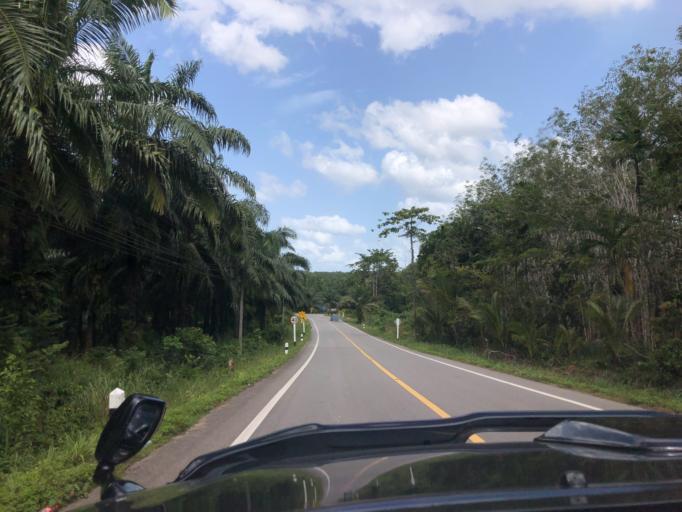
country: TH
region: Krabi
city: Khlong Thom
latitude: 7.9472
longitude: 99.2089
